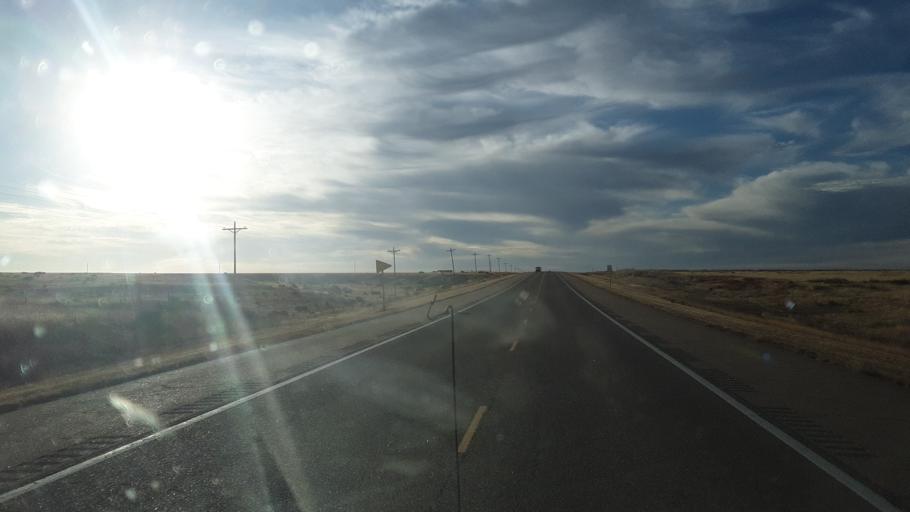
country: US
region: Kansas
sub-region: Kearny County
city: Lakin
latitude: 37.9439
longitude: -101.4528
